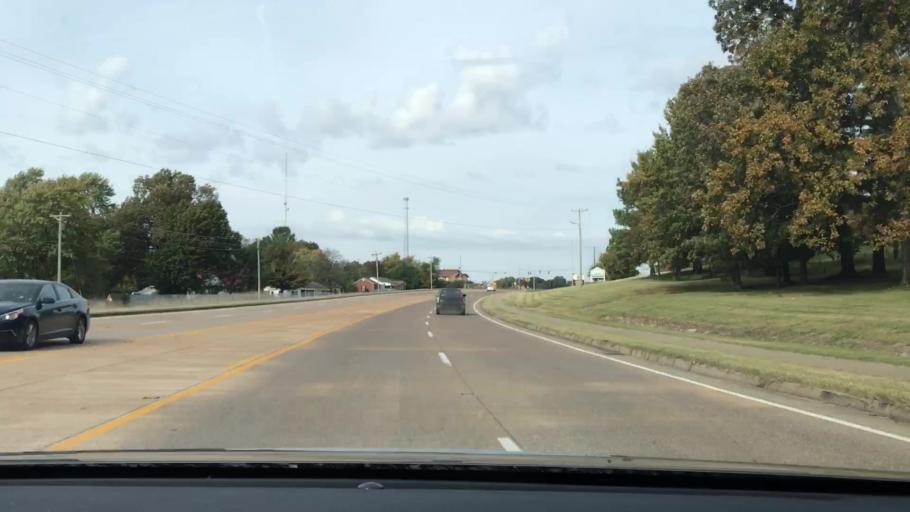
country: US
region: Kentucky
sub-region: Graves County
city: Mayfield
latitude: 36.7528
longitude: -88.6515
